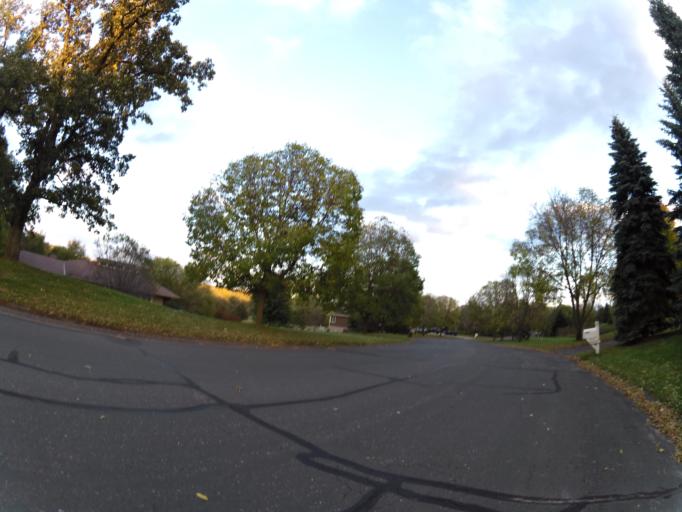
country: US
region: Minnesota
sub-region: Washington County
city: Lake Elmo
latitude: 44.9617
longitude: -92.8276
